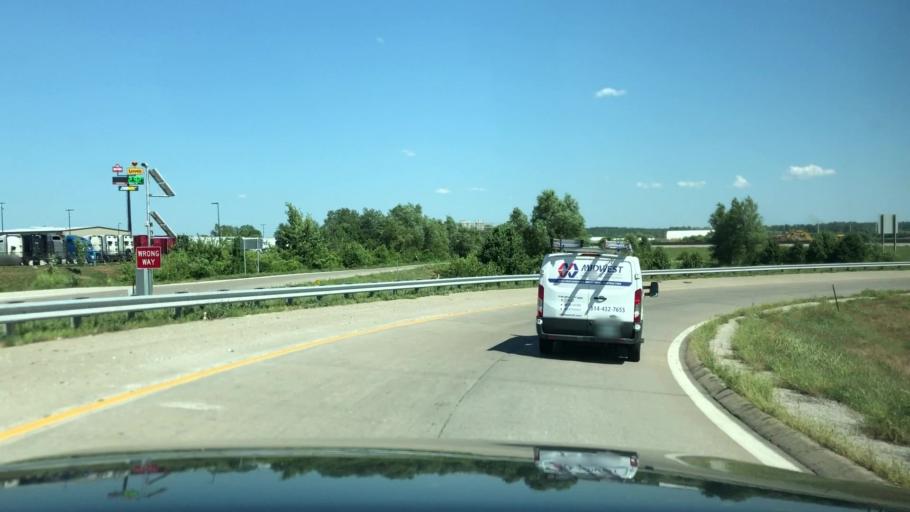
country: US
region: Missouri
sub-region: Saint Charles County
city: Saint Charles
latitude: 38.7934
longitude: -90.4502
